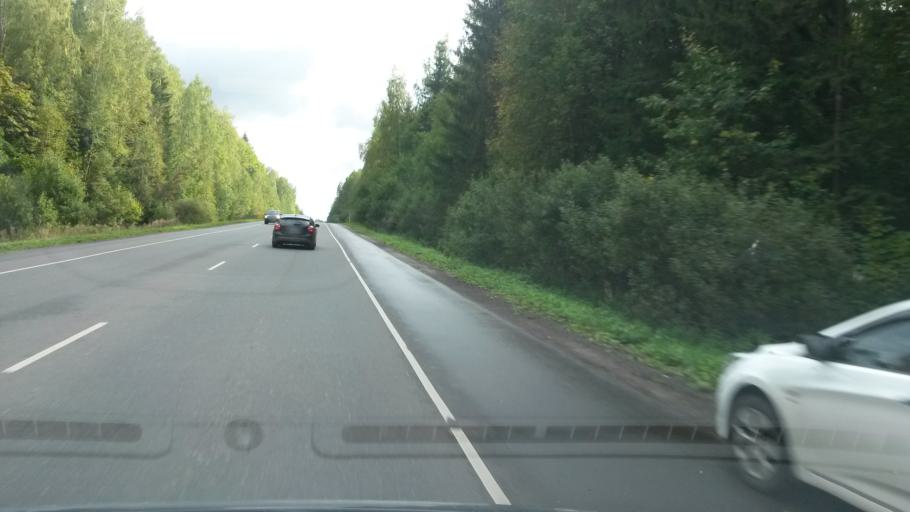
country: RU
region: Ivanovo
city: Kaminskiy
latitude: 57.0842
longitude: 41.5719
